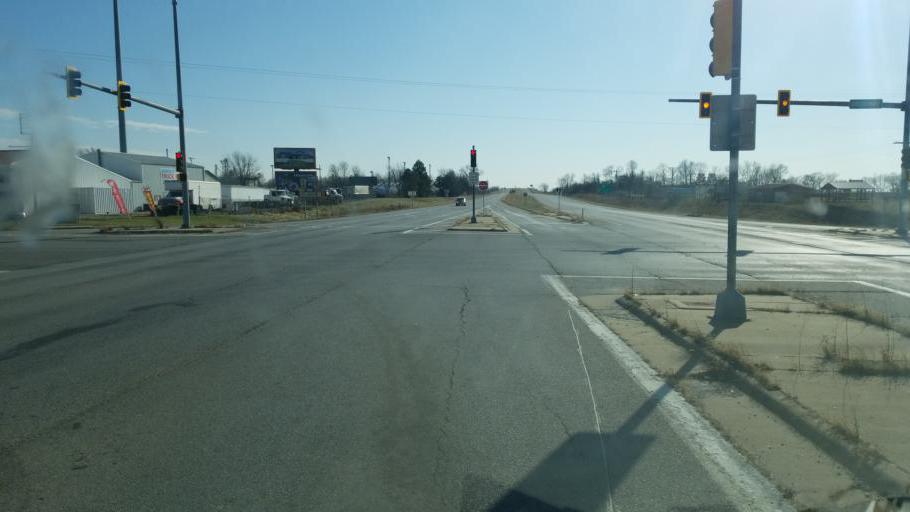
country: US
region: Illinois
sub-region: Warren County
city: Monmouth
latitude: 40.9126
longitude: -90.6630
